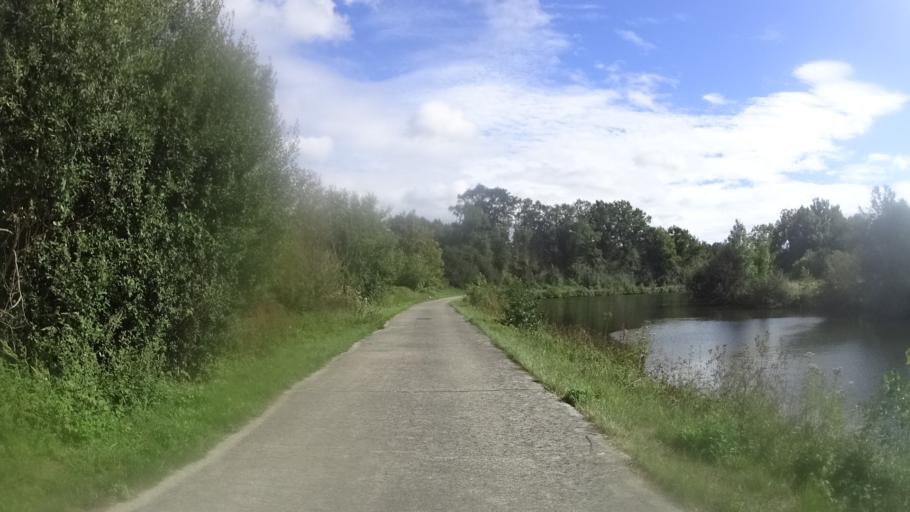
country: BE
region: Wallonia
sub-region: Province du Hainaut
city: Merbes-le-Chateau
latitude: 50.3248
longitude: 4.2175
